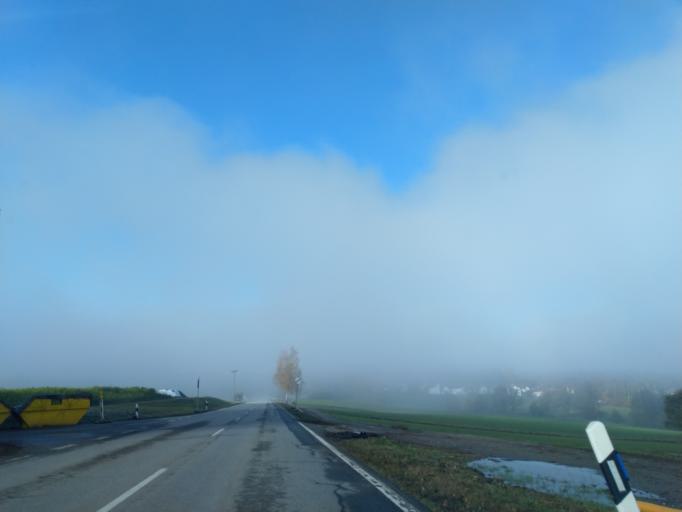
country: DE
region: Bavaria
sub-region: Lower Bavaria
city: Aussernzell
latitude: 48.7201
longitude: 13.2380
